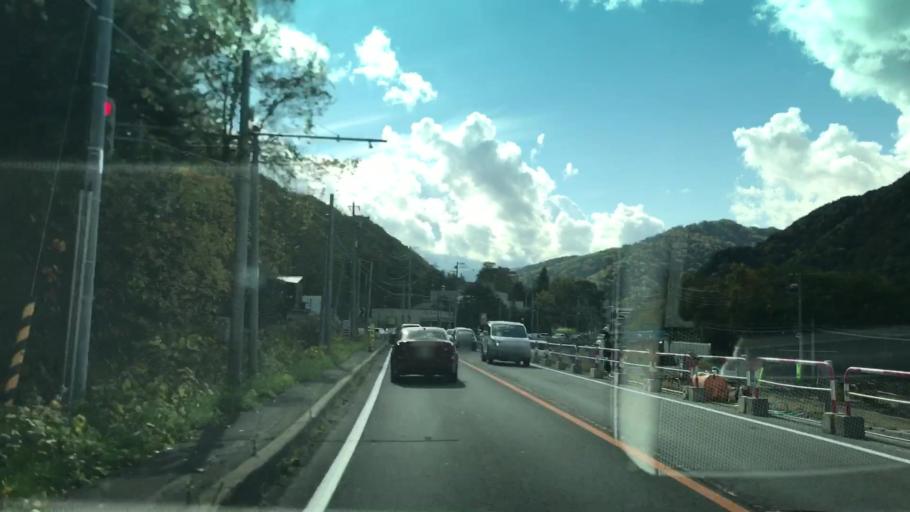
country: JP
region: Hokkaido
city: Sapporo
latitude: 42.9694
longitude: 141.1728
